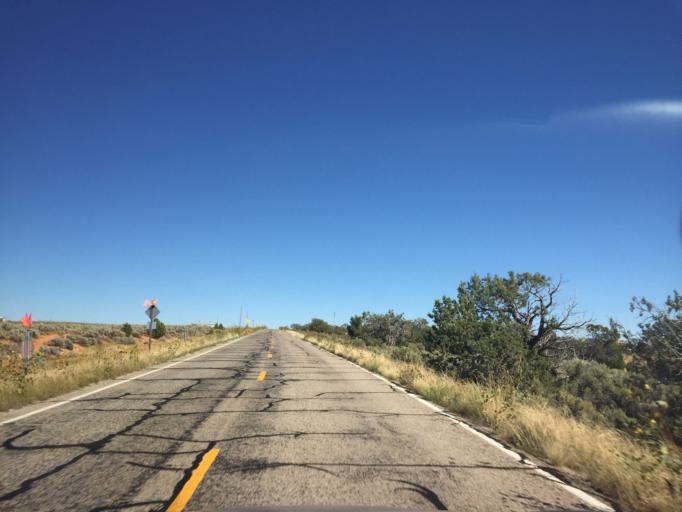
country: US
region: Utah
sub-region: San Juan County
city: Blanding
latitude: 37.5736
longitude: -109.4978
